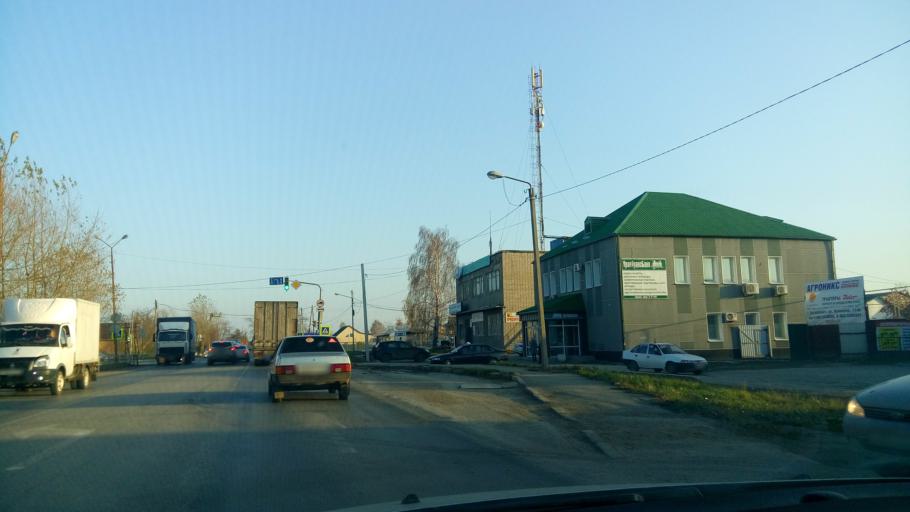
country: RU
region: Sverdlovsk
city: Bogdanovich
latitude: 56.7684
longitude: 62.0511
